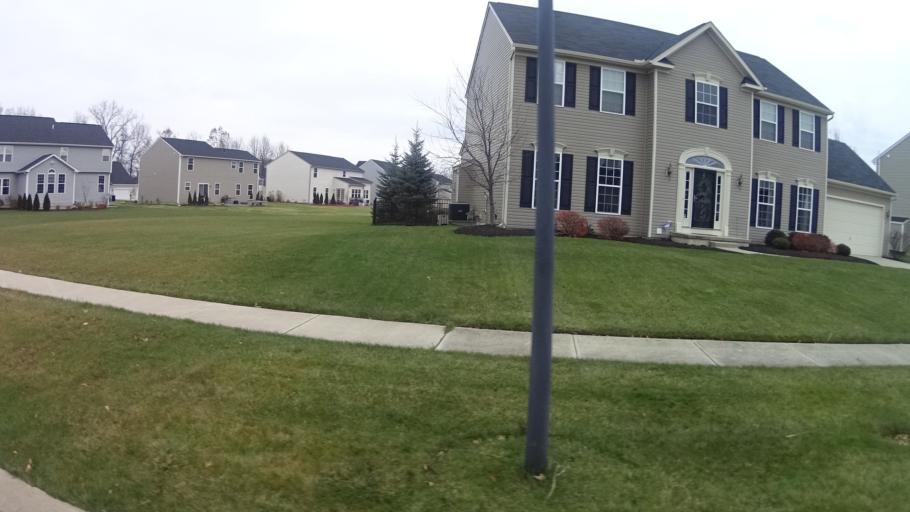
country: US
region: Ohio
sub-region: Lorain County
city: North Ridgeville
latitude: 41.3690
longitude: -81.9755
